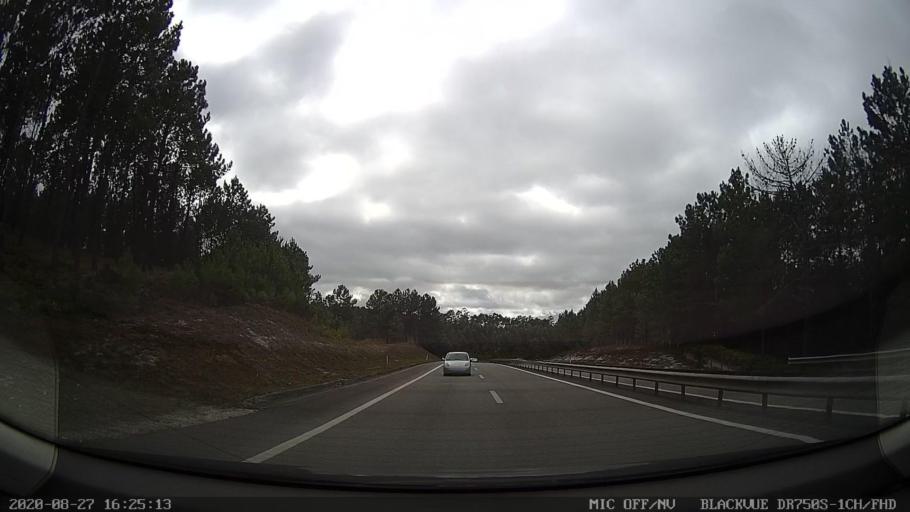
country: PT
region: Leiria
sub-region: Leiria
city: Caranguejeira
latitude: 39.7372
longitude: -8.7471
